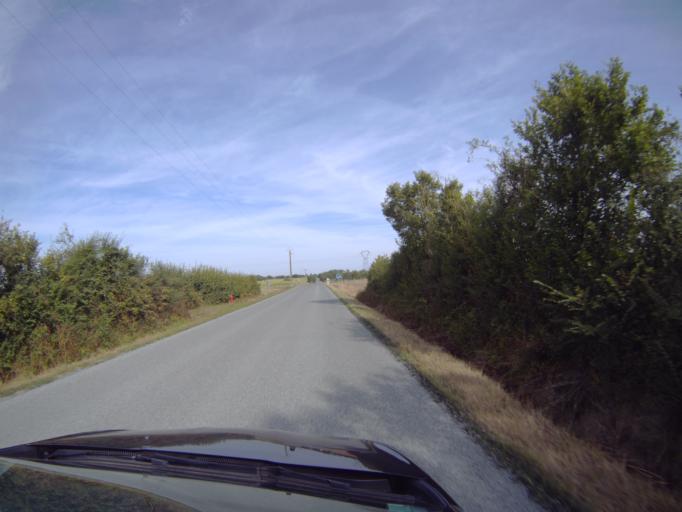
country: FR
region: Pays de la Loire
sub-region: Departement de la Vendee
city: Saint-Andre-Treize-Voies
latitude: 46.9205
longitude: -1.3916
